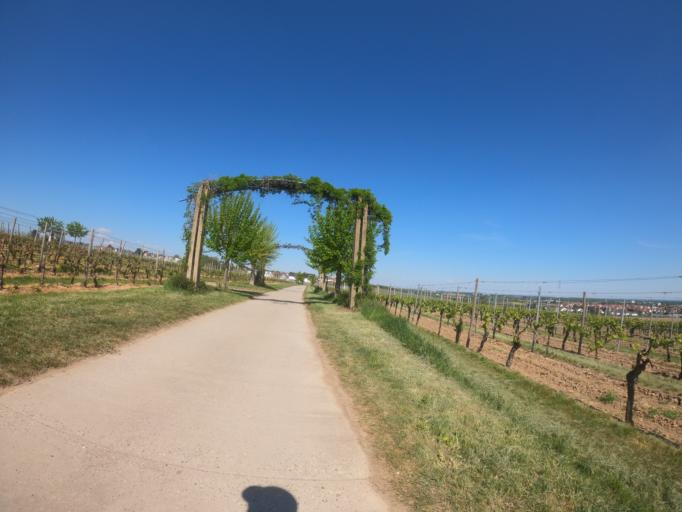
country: DE
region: Hesse
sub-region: Regierungsbezirk Darmstadt
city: Florsheim
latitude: 50.0213
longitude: 8.4055
